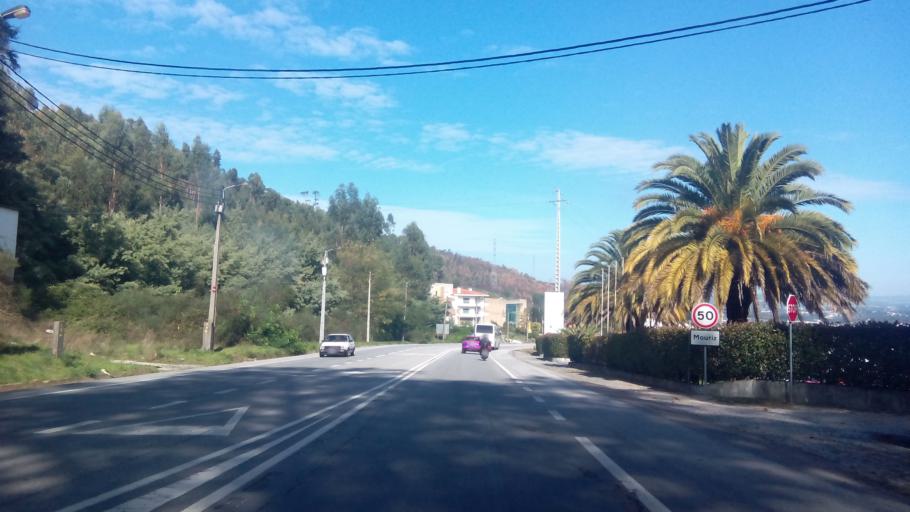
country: PT
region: Porto
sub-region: Paredes
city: Baltar
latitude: 41.1885
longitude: -8.3680
